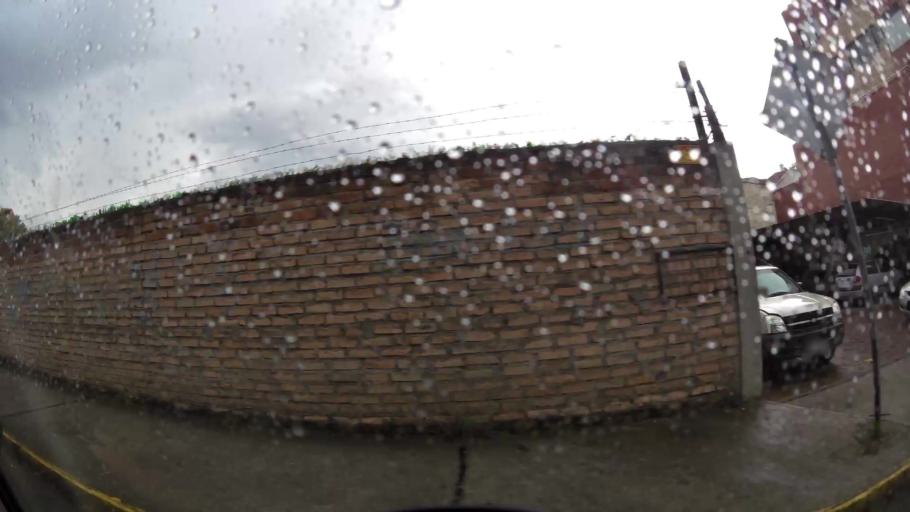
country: EC
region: Azuay
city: Cuenca
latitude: -2.8926
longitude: -79.0221
